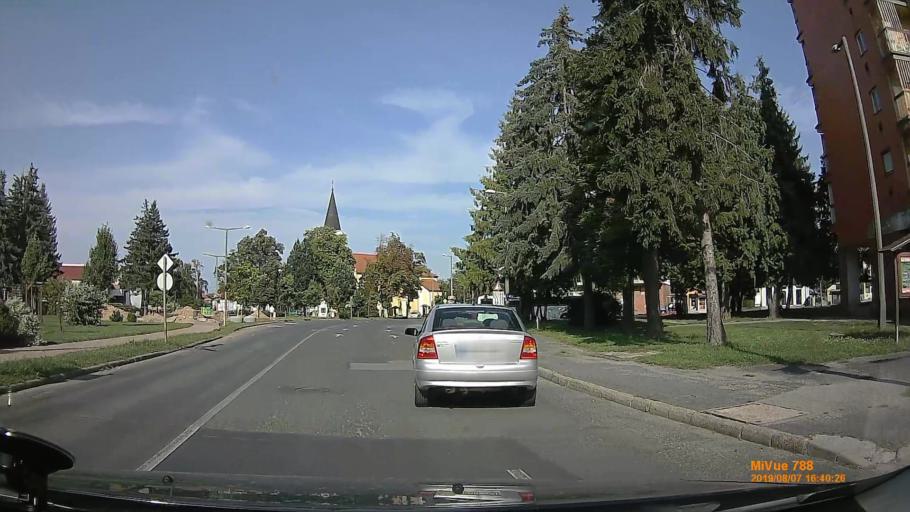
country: HU
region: Zala
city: Lenti
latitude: 46.6231
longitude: 16.5412
